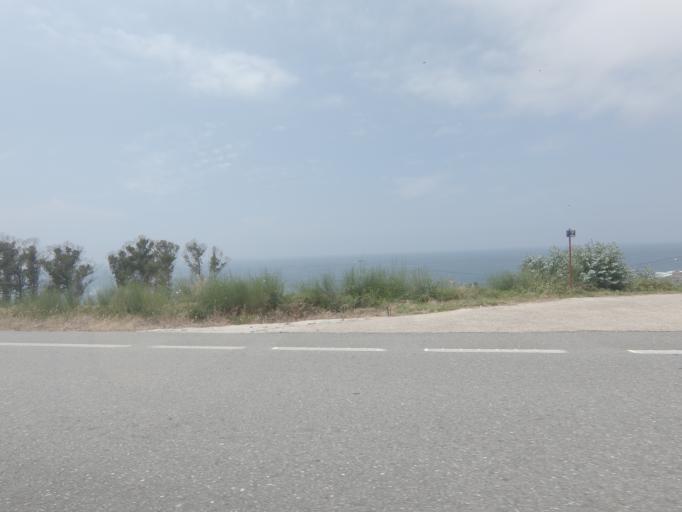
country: ES
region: Galicia
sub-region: Provincia de Pontevedra
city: A Guarda
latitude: 41.9441
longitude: -8.8819
